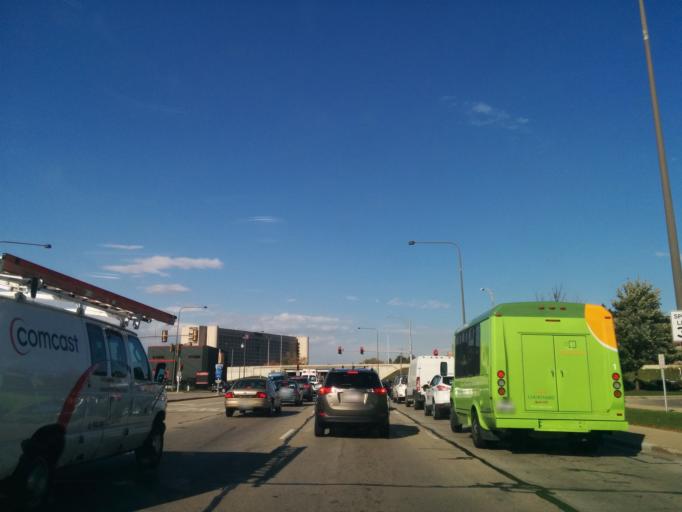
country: US
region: Illinois
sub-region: Cook County
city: Rosemont
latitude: 41.9845
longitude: -87.8612
